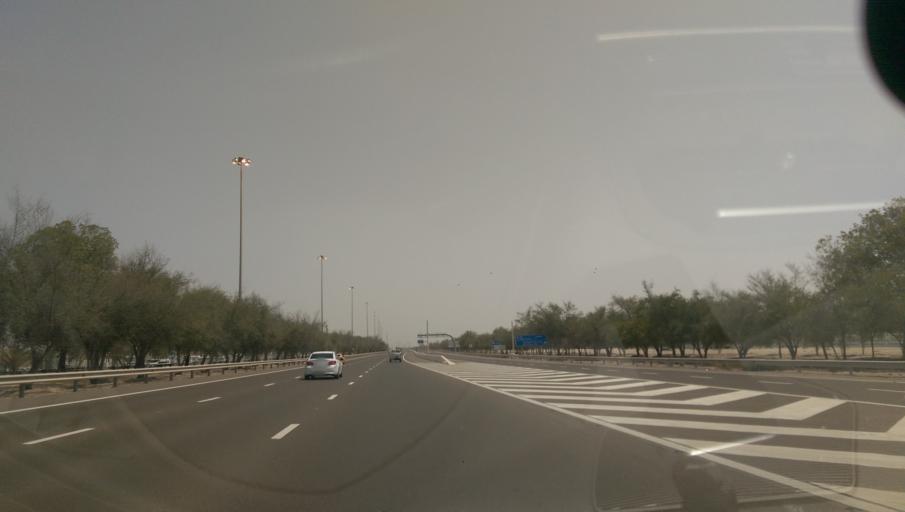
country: AE
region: Abu Dhabi
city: Abu Dhabi
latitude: 24.5309
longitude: 54.6926
